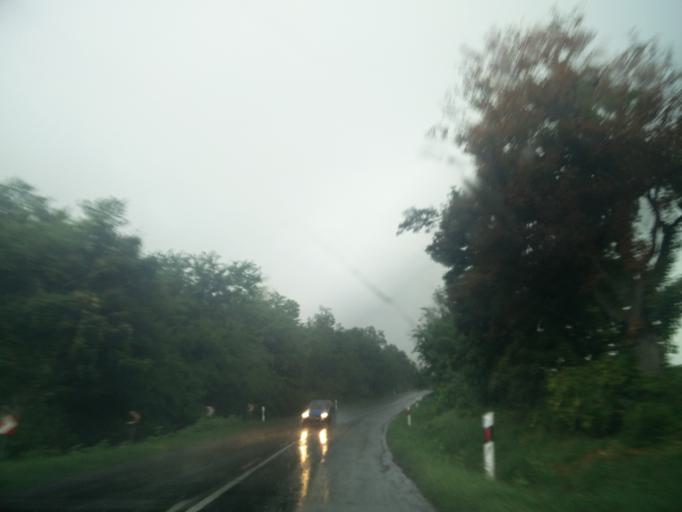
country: HU
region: Fejer
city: Lovasbereny
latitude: 47.3392
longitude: 18.5775
